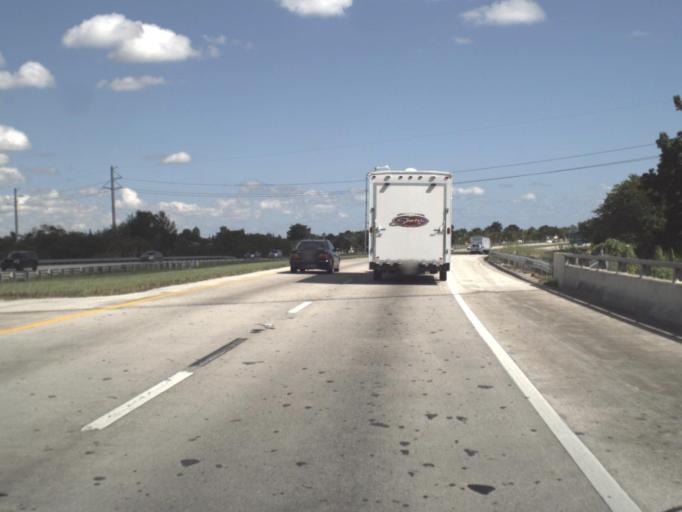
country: US
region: Florida
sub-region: Miami-Dade County
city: Princeton
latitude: 25.5258
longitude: -80.3975
